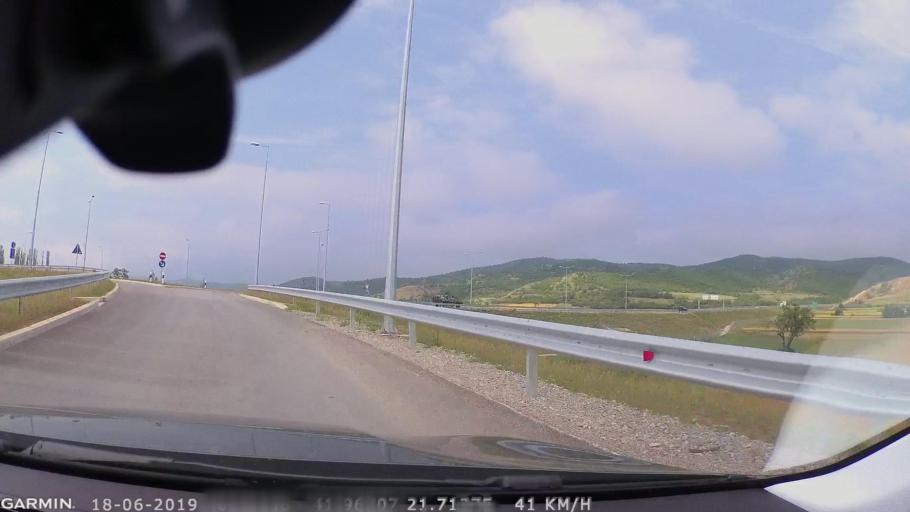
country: MK
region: Petrovec
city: Sredno Konjare
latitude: 41.9447
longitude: 21.8052
